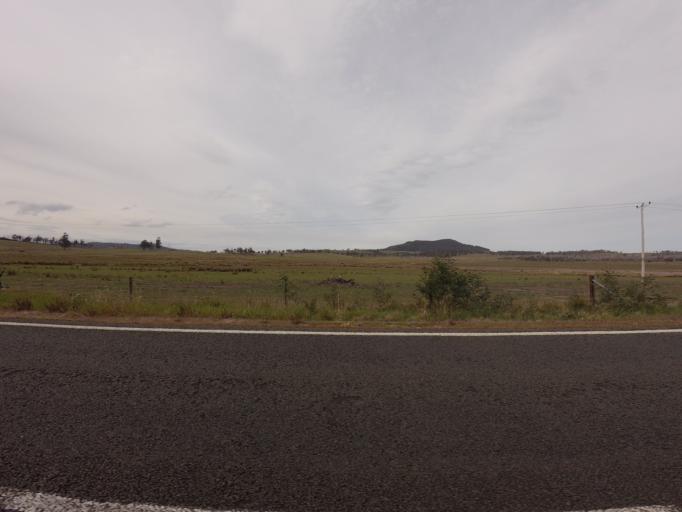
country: AU
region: Tasmania
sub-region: Sorell
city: Sorell
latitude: -42.4765
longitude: 147.9295
